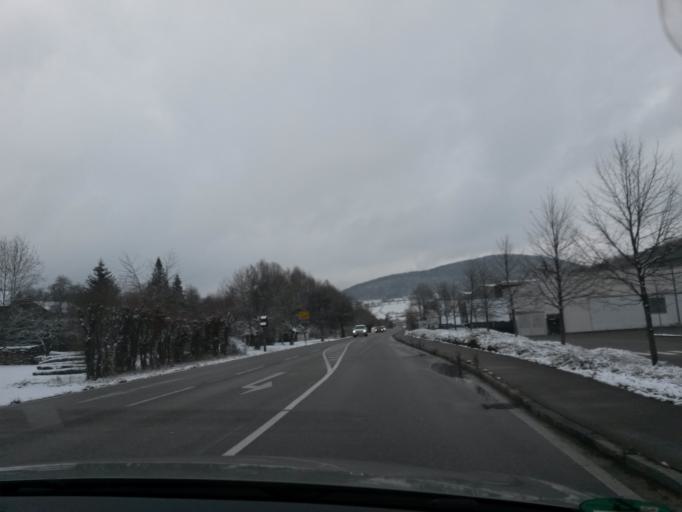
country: DE
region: Baden-Wuerttemberg
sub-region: Regierungsbezirk Stuttgart
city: Deggingen
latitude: 48.5999
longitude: 9.7261
